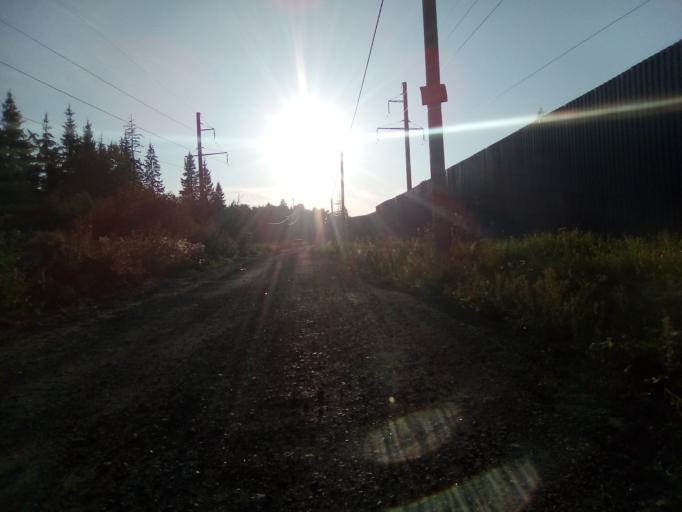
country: RU
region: Moskovskaya
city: Krasnoznamensk
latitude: 55.5808
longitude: 37.0549
